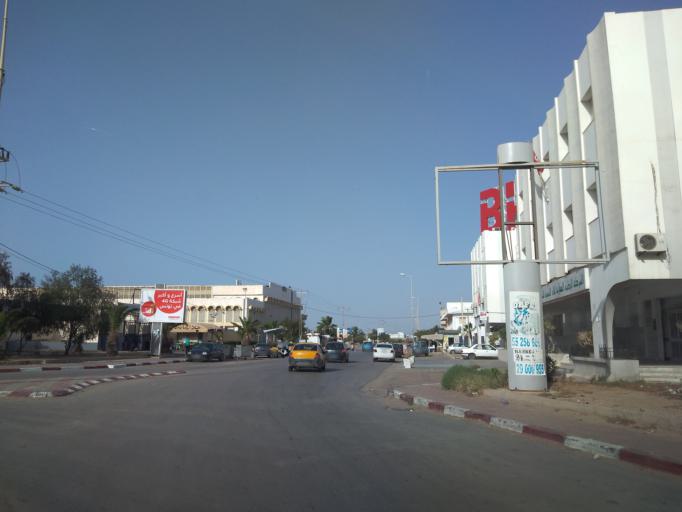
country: TN
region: Safaqis
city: Sfax
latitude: 34.7291
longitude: 10.7537
